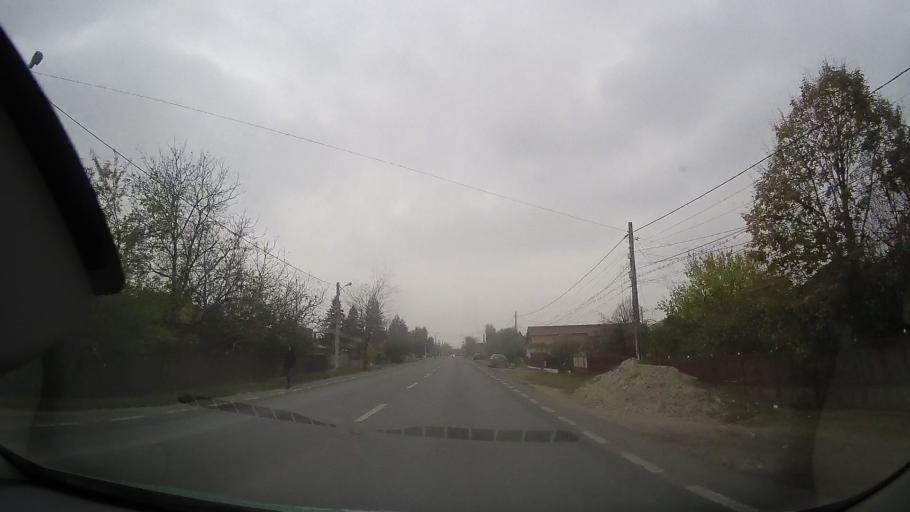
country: RO
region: Ialomita
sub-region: Comuna Manasia
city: Manasia
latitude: 44.7101
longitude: 26.6639
